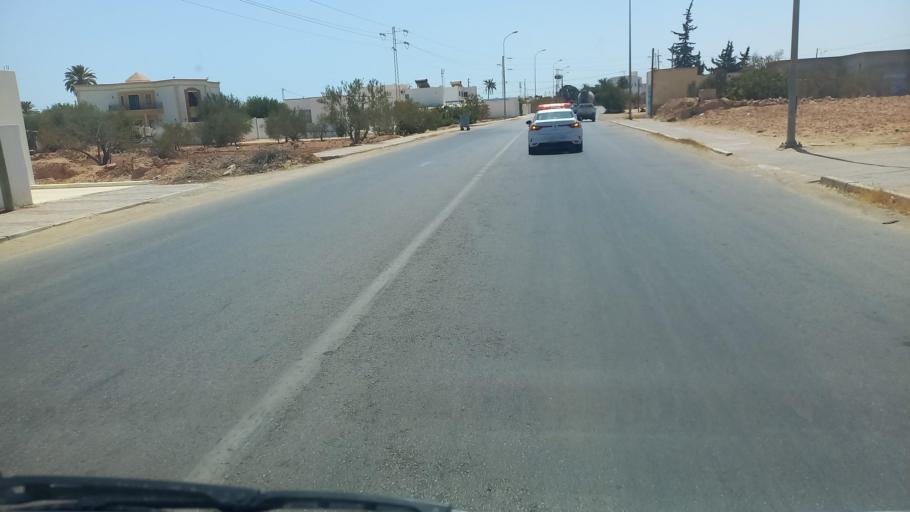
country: TN
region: Madanin
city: Houmt Souk
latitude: 33.7794
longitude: 10.8915
